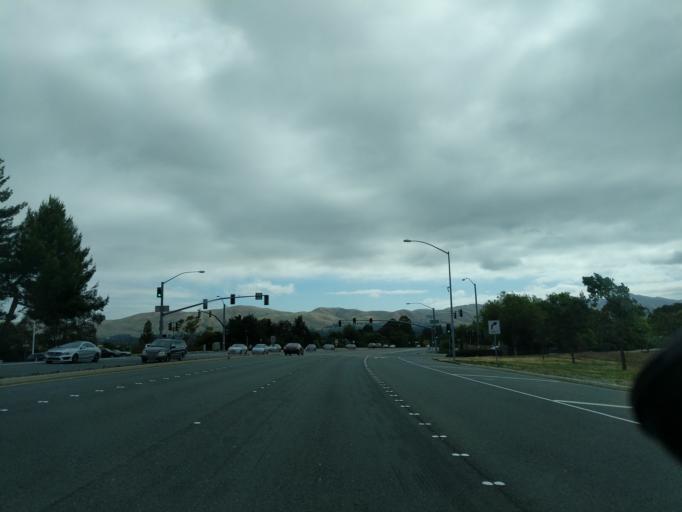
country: US
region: California
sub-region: Contra Costa County
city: Concord
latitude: 37.9464
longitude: -121.9932
